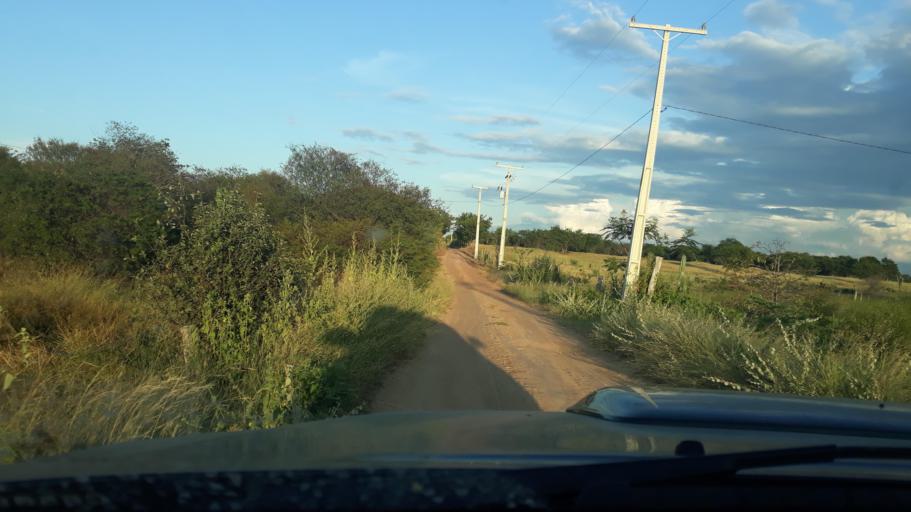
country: BR
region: Bahia
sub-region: Riacho De Santana
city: Riacho de Santana
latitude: -13.8632
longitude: -43.0230
